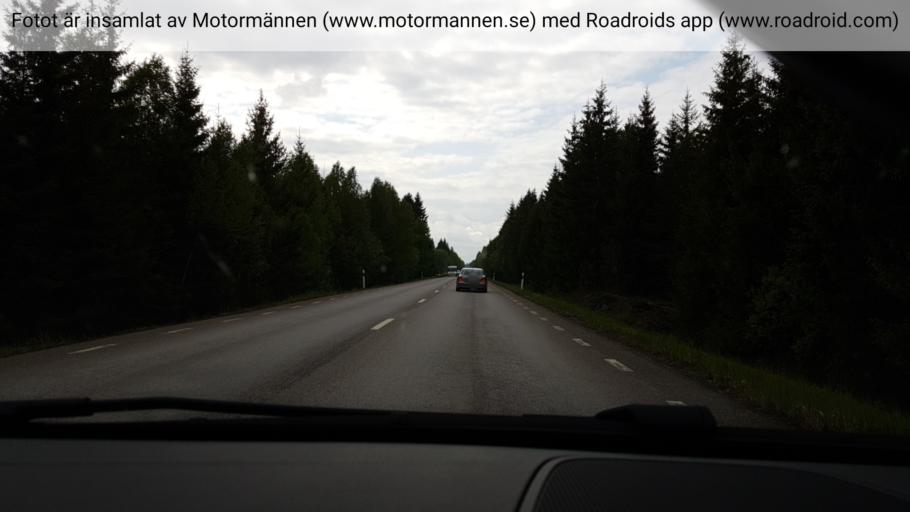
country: SE
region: Uppsala
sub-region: Osthammars Kommun
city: Gimo
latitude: 60.1637
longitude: 18.0930
